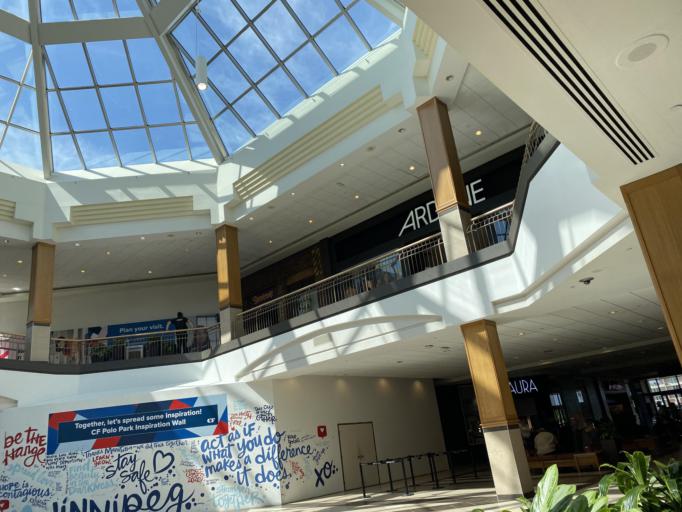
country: CA
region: Manitoba
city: Winnipeg
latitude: 49.8831
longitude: -97.1991
